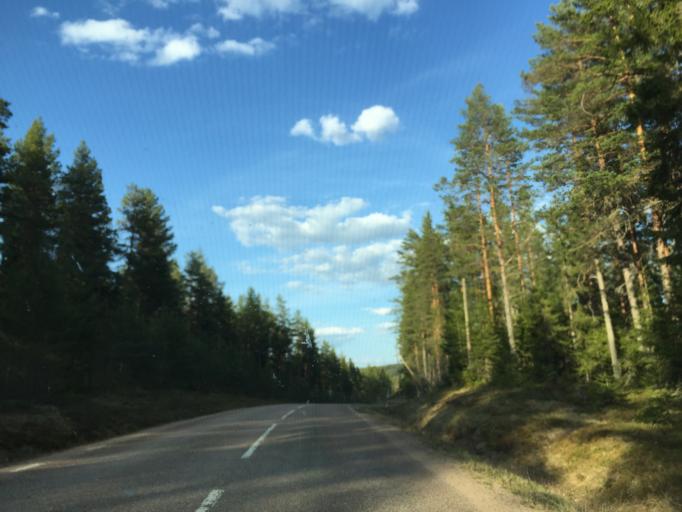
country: SE
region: Dalarna
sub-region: Vansbro Kommun
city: Jarna
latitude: 60.5649
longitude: 14.4250
